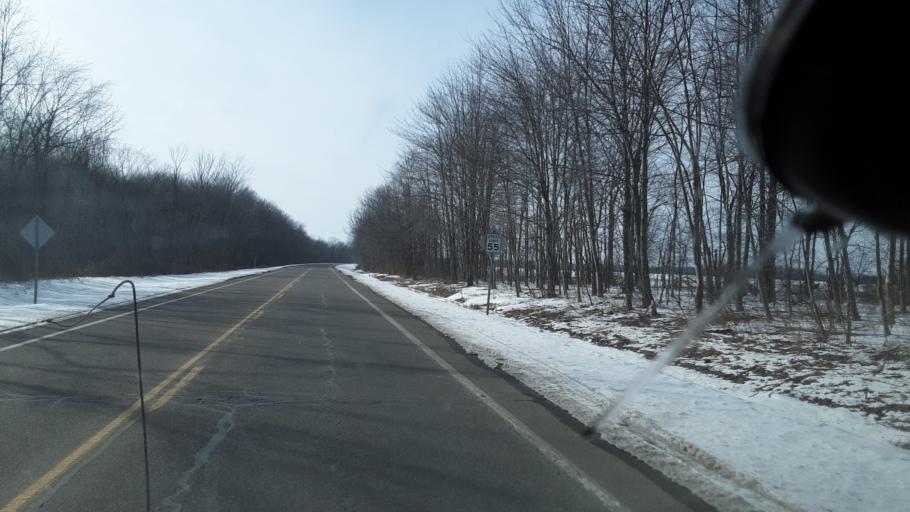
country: US
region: Ohio
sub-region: Stark County
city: Alliance
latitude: 41.0313
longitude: -81.1503
